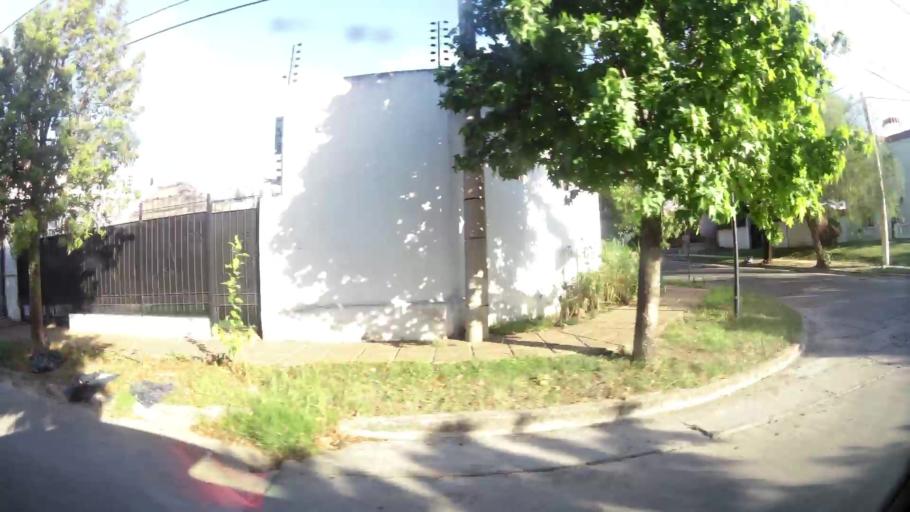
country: AR
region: Cordoba
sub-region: Departamento de Capital
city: Cordoba
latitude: -31.3868
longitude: -64.2386
